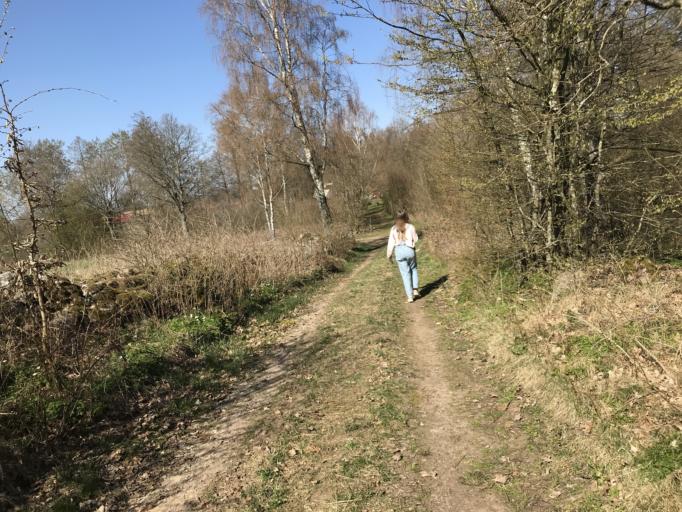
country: SE
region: Skane
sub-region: Eslovs Kommun
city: Stehag
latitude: 56.0120
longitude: 13.3810
